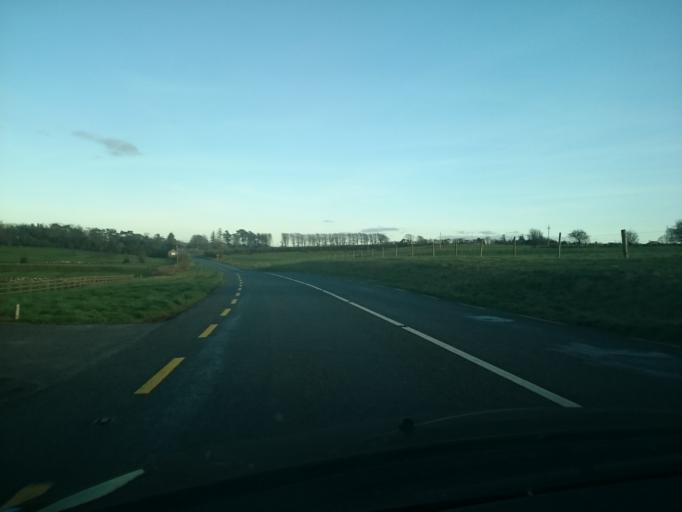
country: IE
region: Connaught
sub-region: Maigh Eo
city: Kiltamagh
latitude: 53.7836
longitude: -9.0816
